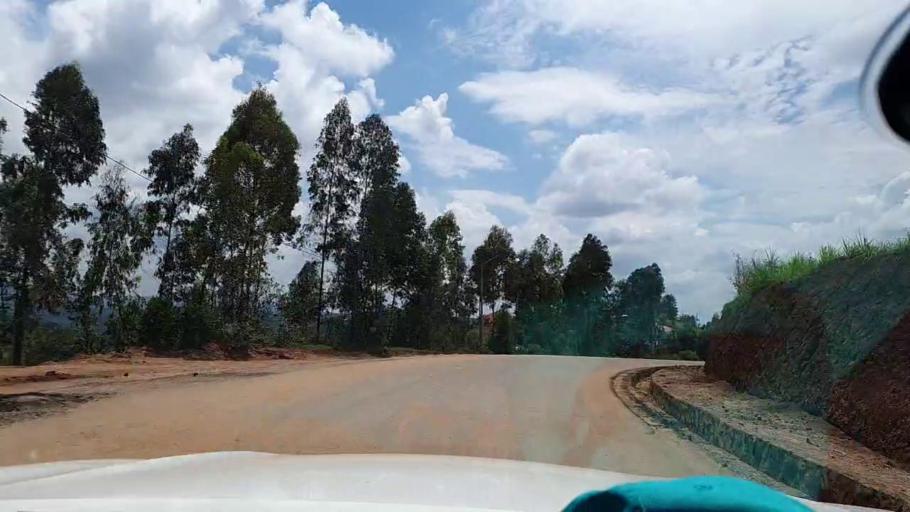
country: RW
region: Southern Province
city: Nzega
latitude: -2.6531
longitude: 29.5580
